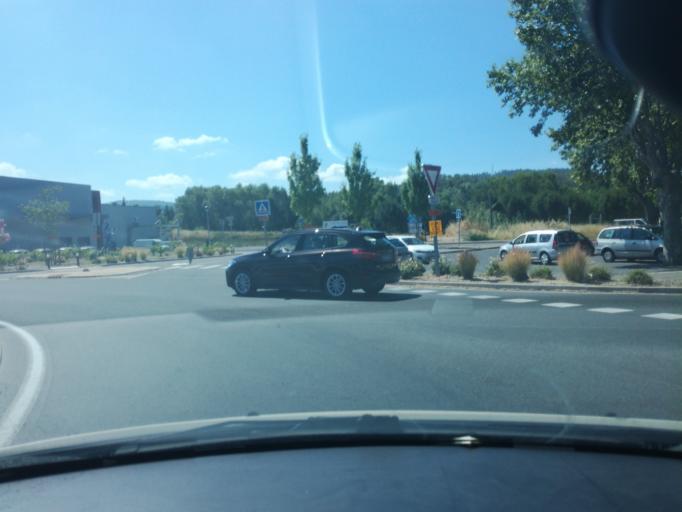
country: FR
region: Provence-Alpes-Cote d'Azur
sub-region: Departement du Var
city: Les Arcs
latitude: 43.4474
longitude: 6.4745
